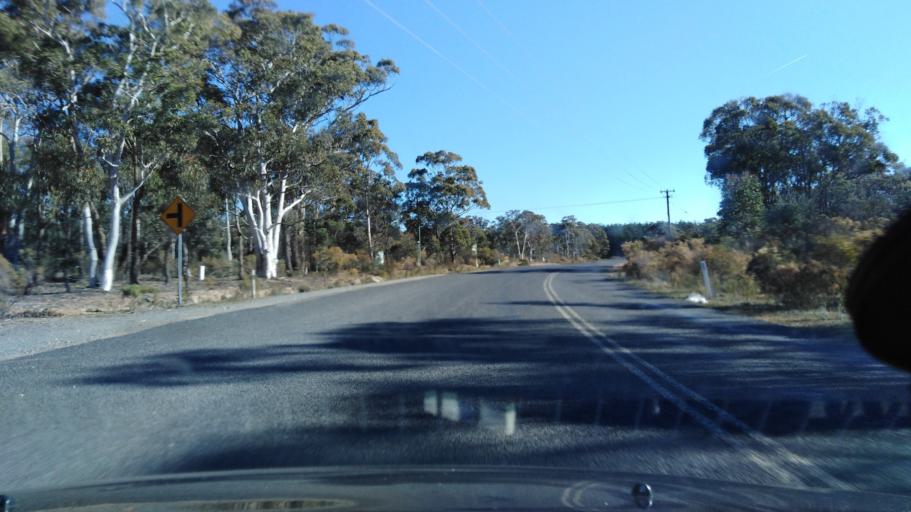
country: AU
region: New South Wales
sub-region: Palerang
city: Bungendore
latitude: -35.2088
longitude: 149.3429
